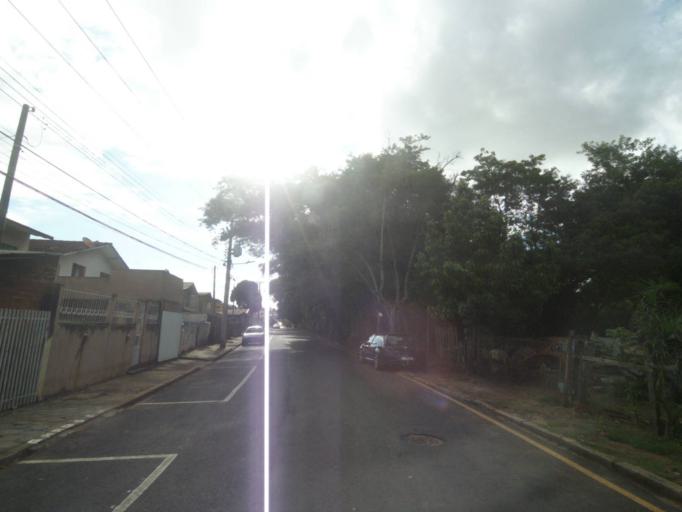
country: BR
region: Parana
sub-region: Telemaco Borba
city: Telemaco Borba
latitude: -24.3351
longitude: -50.6123
